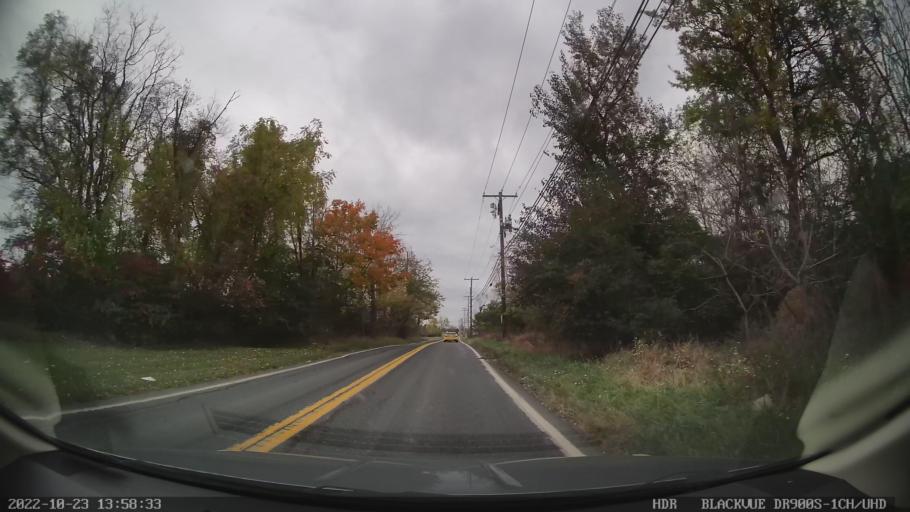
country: US
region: Pennsylvania
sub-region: Northampton County
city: Northampton
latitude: 40.6994
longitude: -75.4689
